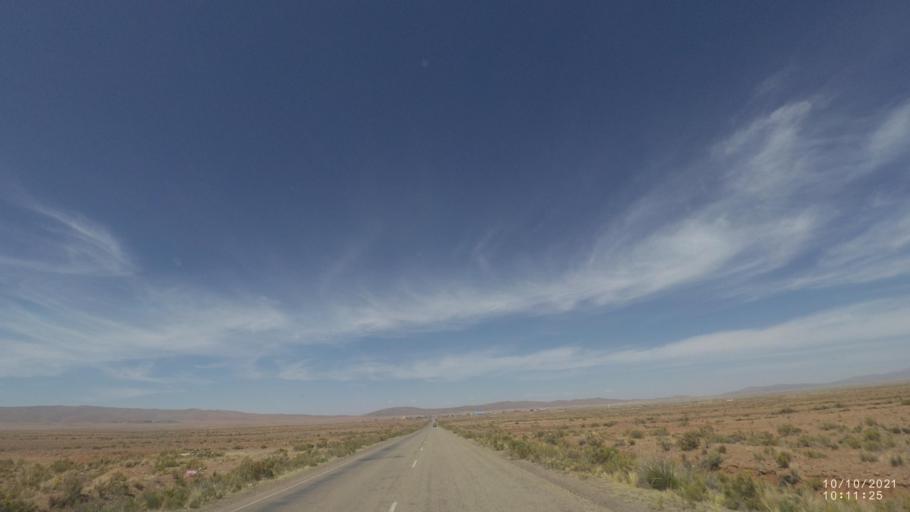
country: BO
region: La Paz
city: Eucaliptus
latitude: -17.4225
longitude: -67.5035
